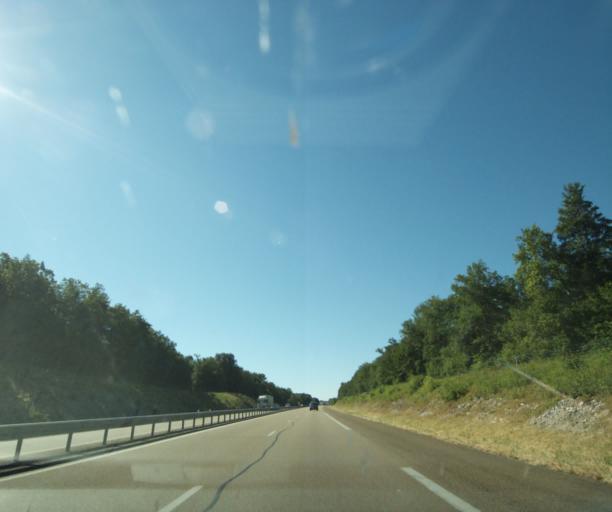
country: FR
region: Champagne-Ardenne
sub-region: Departement de la Haute-Marne
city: Chamarandes-Choignes
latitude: 47.9933
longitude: 5.1238
